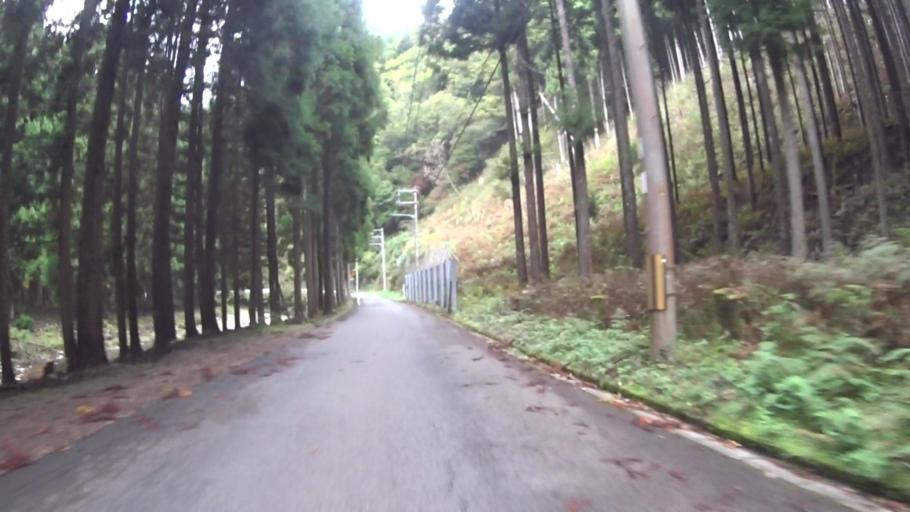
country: JP
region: Fukui
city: Obama
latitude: 35.2965
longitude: 135.6965
